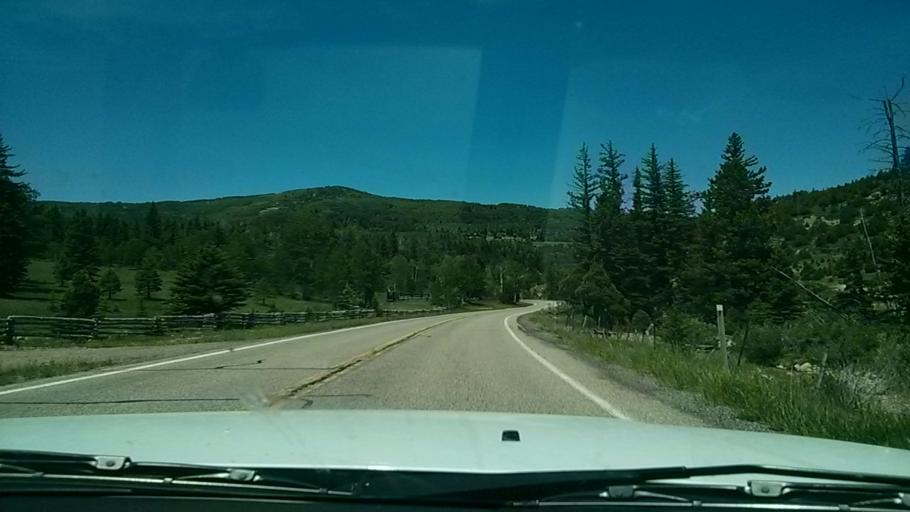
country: US
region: Utah
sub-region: Iron County
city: Cedar City
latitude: 37.5970
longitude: -112.9272
